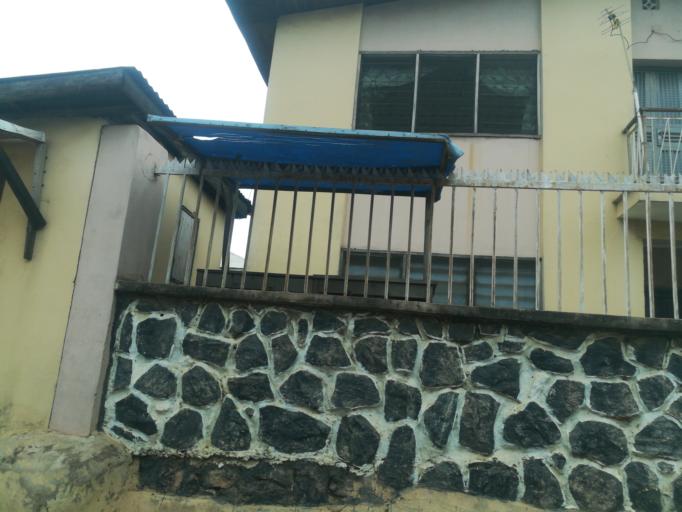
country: NG
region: Oyo
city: Ibadan
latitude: 7.4443
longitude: 3.9111
